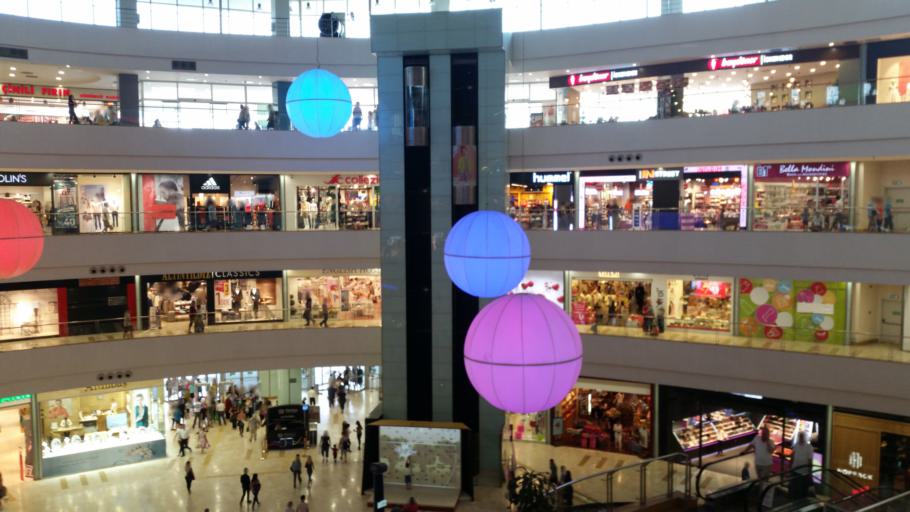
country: TR
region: Tekirdag
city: Tekirdag
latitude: 40.9780
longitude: 27.5039
